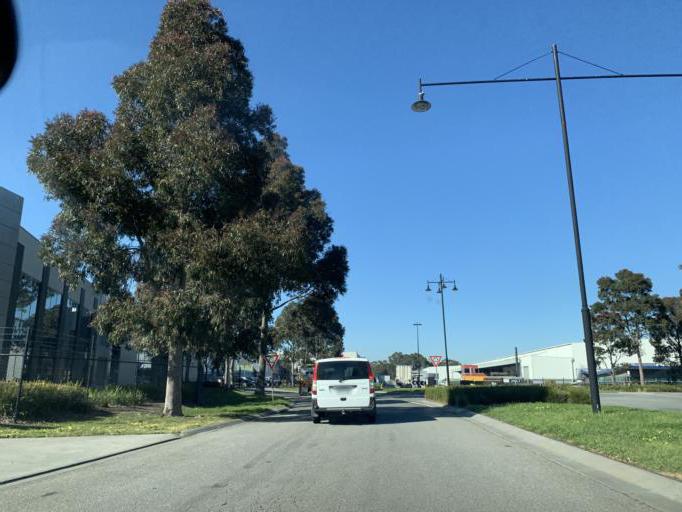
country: AU
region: Victoria
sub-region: Greater Dandenong
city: Dandenong
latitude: -38.0170
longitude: 145.2011
